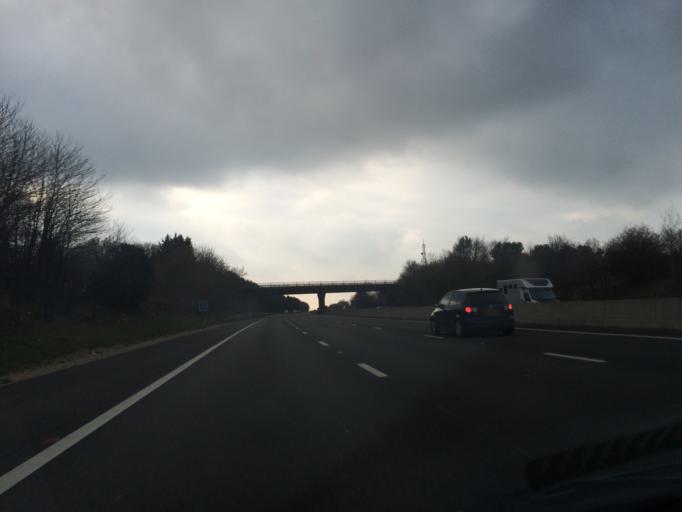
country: GB
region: England
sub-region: West Berkshire
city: Hungerford
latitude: 51.4593
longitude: -1.5000
